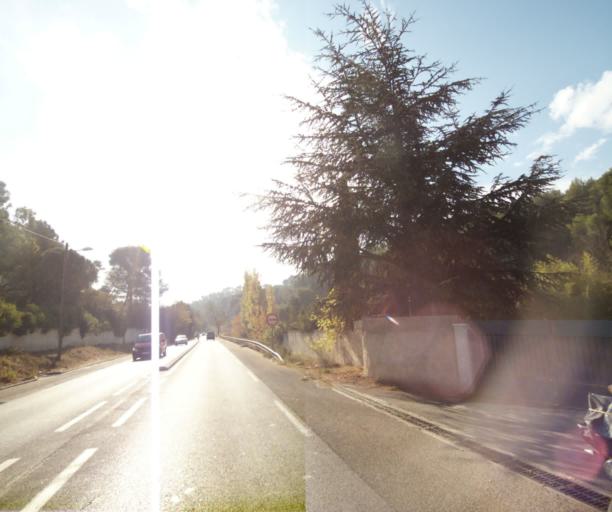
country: FR
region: Provence-Alpes-Cote d'Azur
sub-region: Departement des Bouches-du-Rhone
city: Allauch
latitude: 43.3192
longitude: 5.4944
